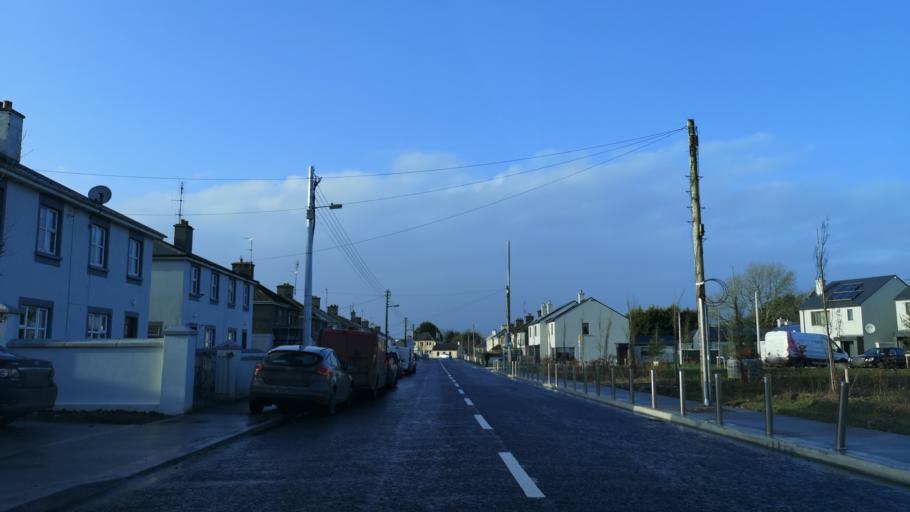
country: IE
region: Connaught
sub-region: County Galway
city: Tuam
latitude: 53.5102
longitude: -8.8582
